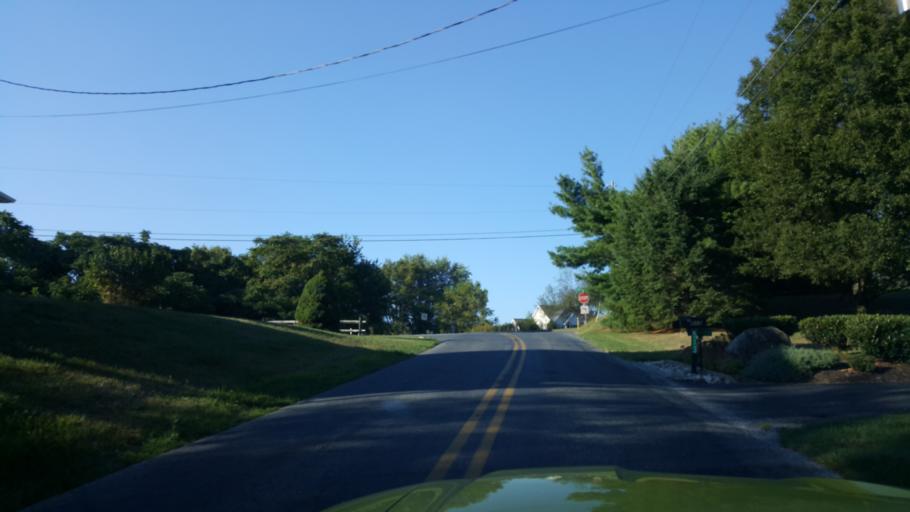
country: US
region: Pennsylvania
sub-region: Lancaster County
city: Rheems
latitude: 40.1638
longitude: -76.5446
